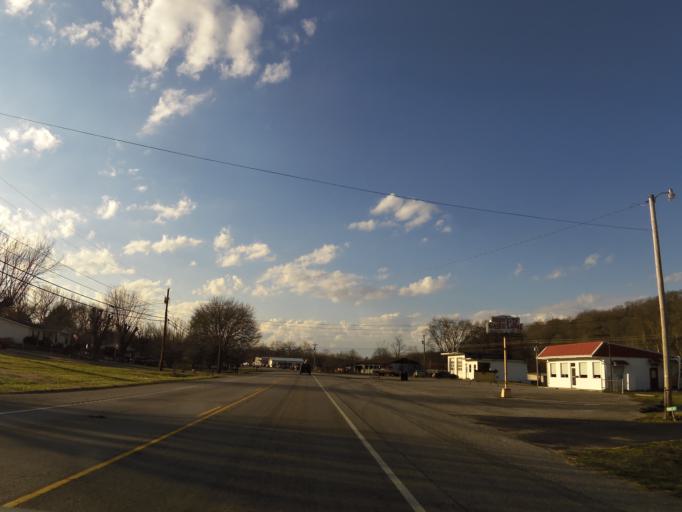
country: US
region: Tennessee
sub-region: Smith County
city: Carthage
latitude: 36.2612
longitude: -86.0508
